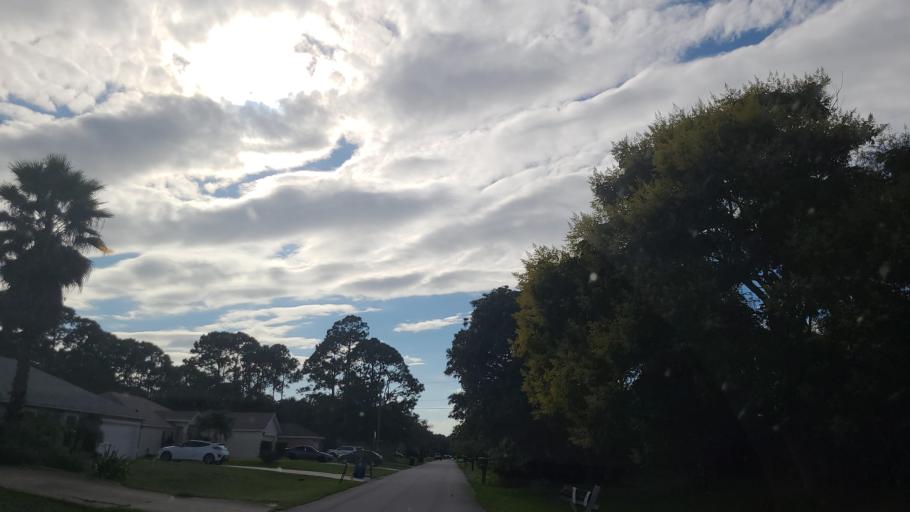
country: US
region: Florida
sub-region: Brevard County
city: Grant-Valkaria
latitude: 27.9705
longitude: -80.6656
